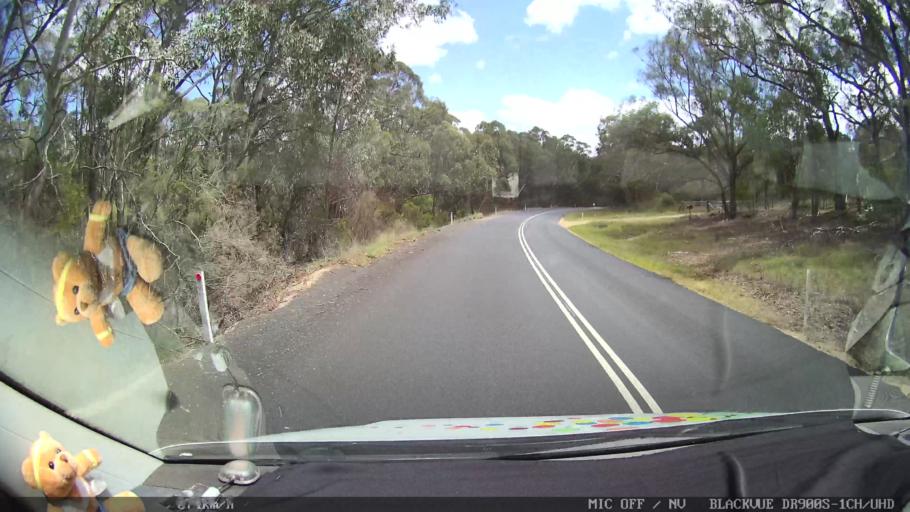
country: AU
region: New South Wales
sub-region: Glen Innes Severn
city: Glen Innes
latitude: -29.5569
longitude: 151.6663
